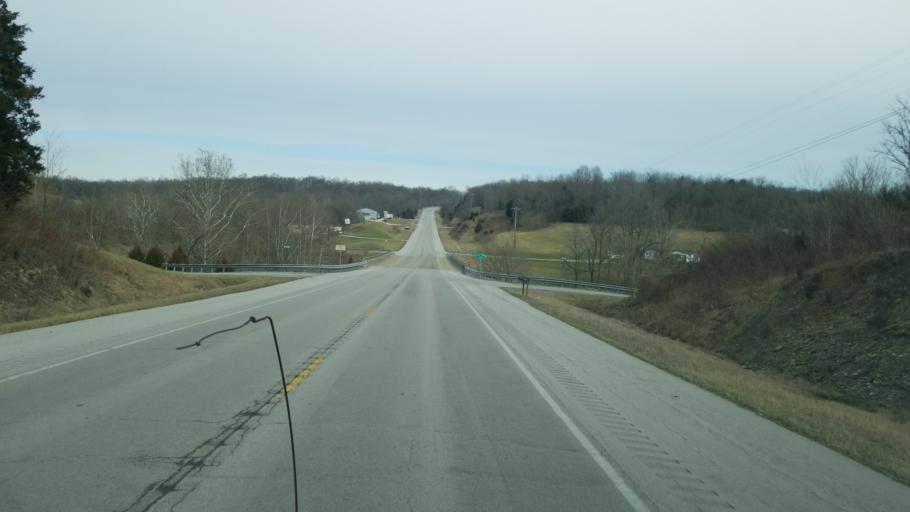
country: US
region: Kentucky
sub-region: Robertson County
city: Mount Olivet
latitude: 38.4720
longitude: -83.9059
